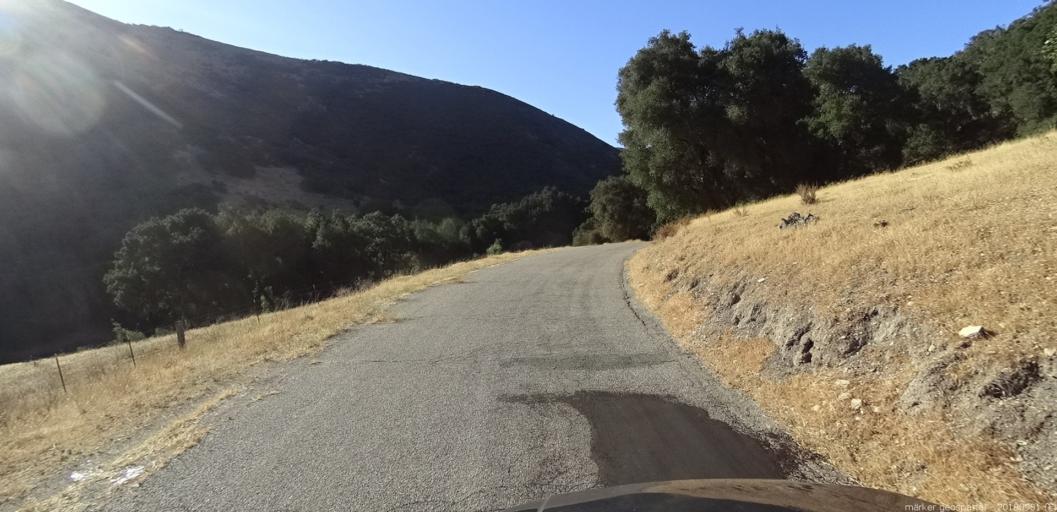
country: US
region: California
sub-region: Monterey County
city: Greenfield
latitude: 36.1999
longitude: -121.2763
